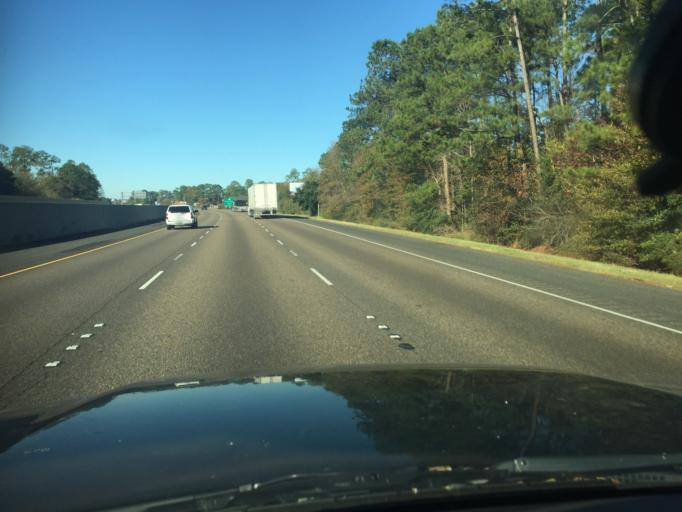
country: US
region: Louisiana
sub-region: Saint Tammany Parish
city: Slidell
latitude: 30.3093
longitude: -89.7517
